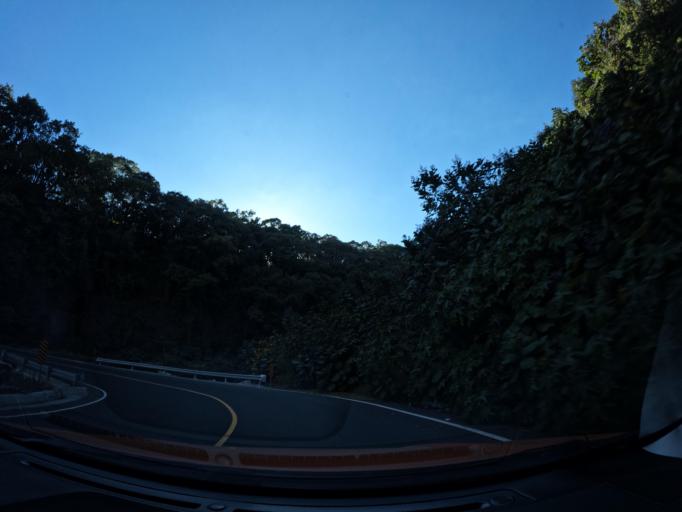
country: GT
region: Escuintla
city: Palin
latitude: 14.4588
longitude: -90.6961
